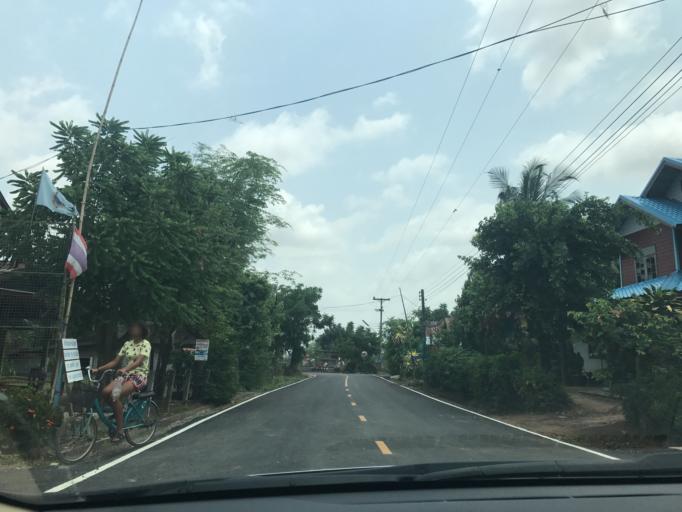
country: TH
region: Surin
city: Khwao Sinarin
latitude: 15.0397
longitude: 103.6507
